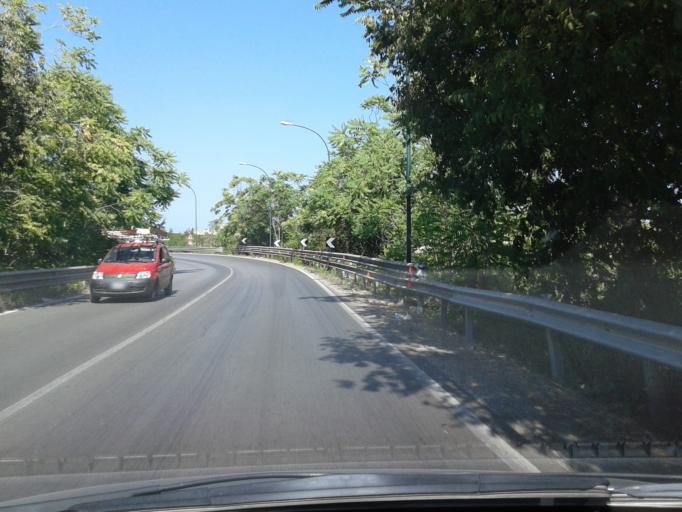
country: IT
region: Sicily
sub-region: Palermo
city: Monreale
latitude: 38.0908
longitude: 13.3058
